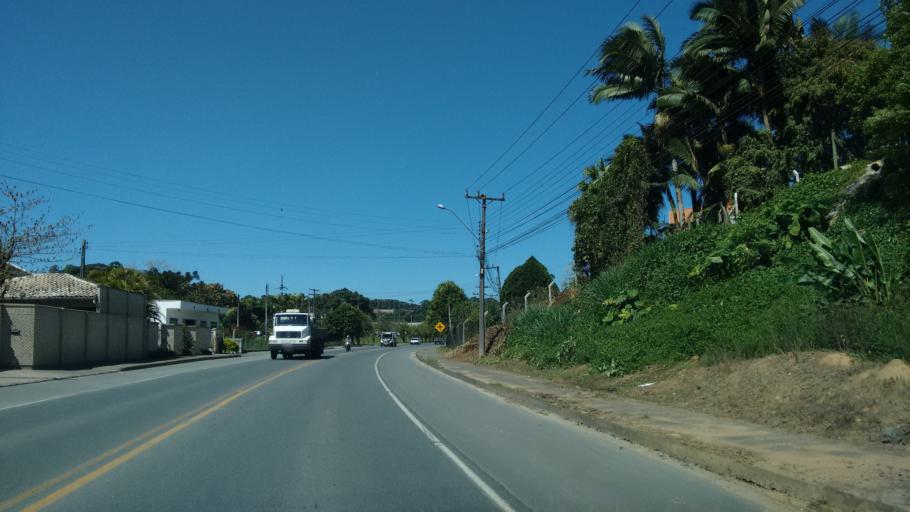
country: BR
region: Santa Catarina
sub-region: Indaial
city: Indaial
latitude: -26.8460
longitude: -49.1561
